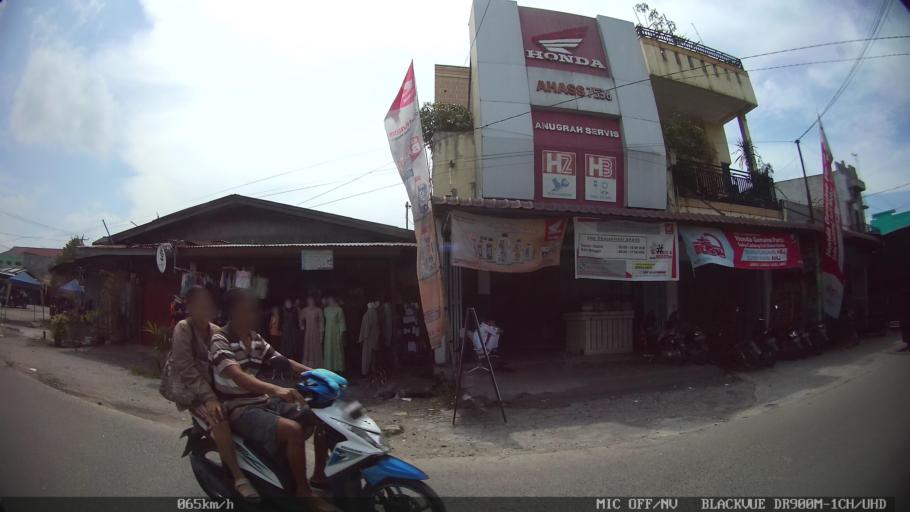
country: ID
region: North Sumatra
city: Labuhan Deli
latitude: 3.6582
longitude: 98.6768
